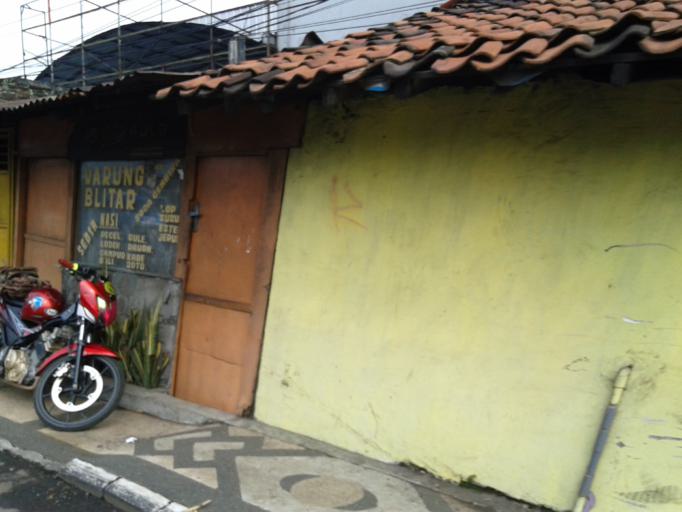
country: ID
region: East Java
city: Singosari
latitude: -7.9239
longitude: 112.6518
